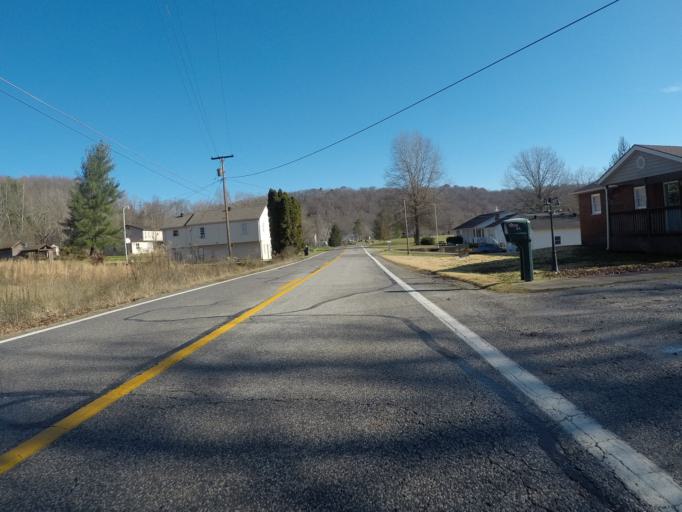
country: US
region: West Virginia
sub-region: Cabell County
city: Huntington
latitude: 38.4694
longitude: -82.4407
